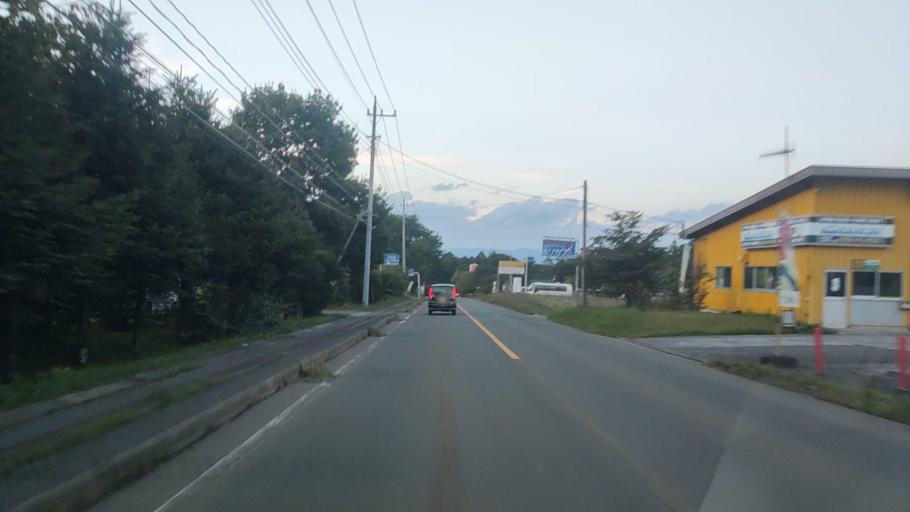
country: JP
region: Nagano
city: Komoro
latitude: 36.4755
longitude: 138.5866
